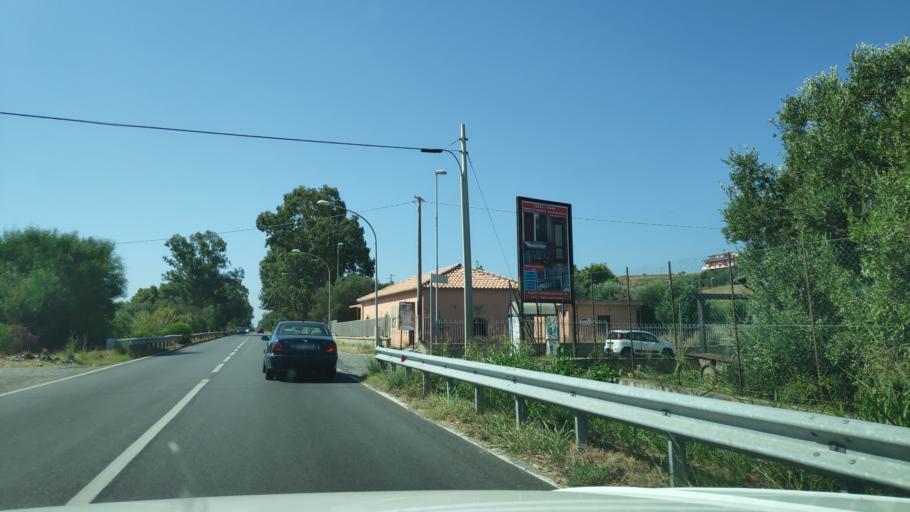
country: IT
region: Calabria
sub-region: Provincia di Reggio Calabria
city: Bianco
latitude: 38.1230
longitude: 16.1592
